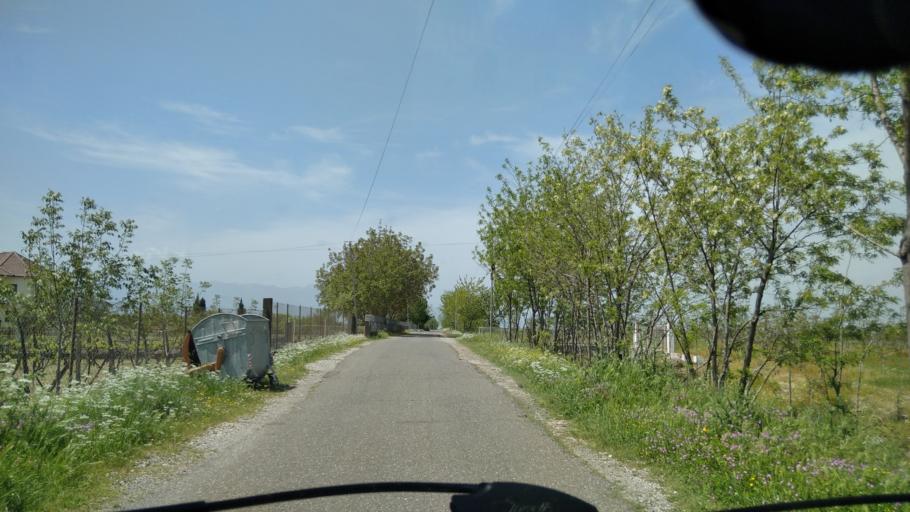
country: AL
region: Shkoder
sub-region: Rrethi i Malesia e Madhe
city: Gruemire
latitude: 42.1424
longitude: 19.5180
